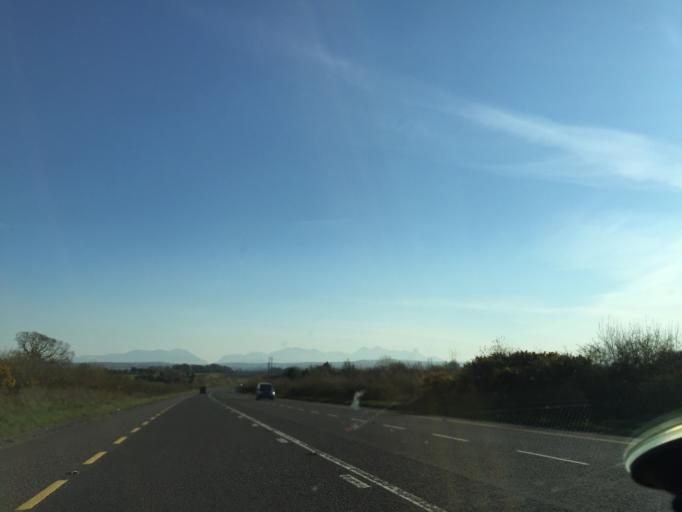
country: IE
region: Munster
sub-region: Ciarrai
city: Castleisland
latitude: 52.2108
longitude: -9.5659
